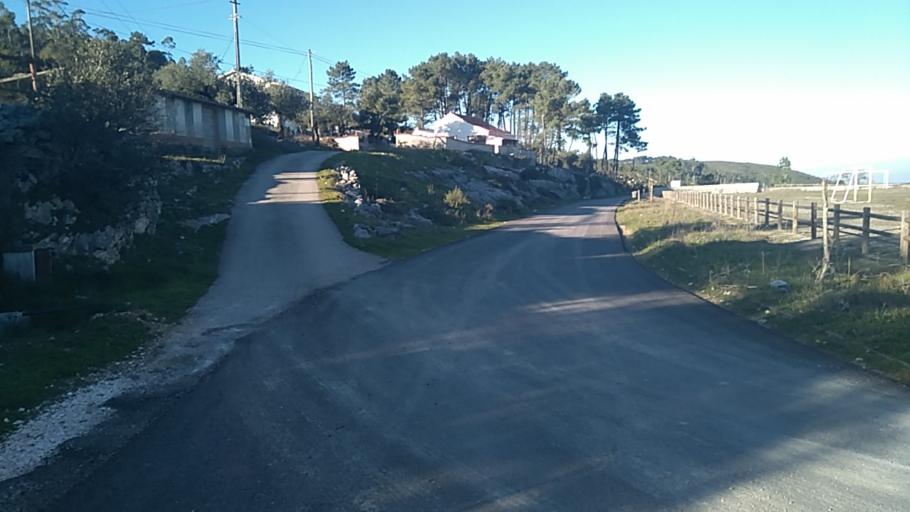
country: PT
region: Leiria
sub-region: Porto de Mos
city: Porto de Mos
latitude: 39.5529
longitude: -8.8440
